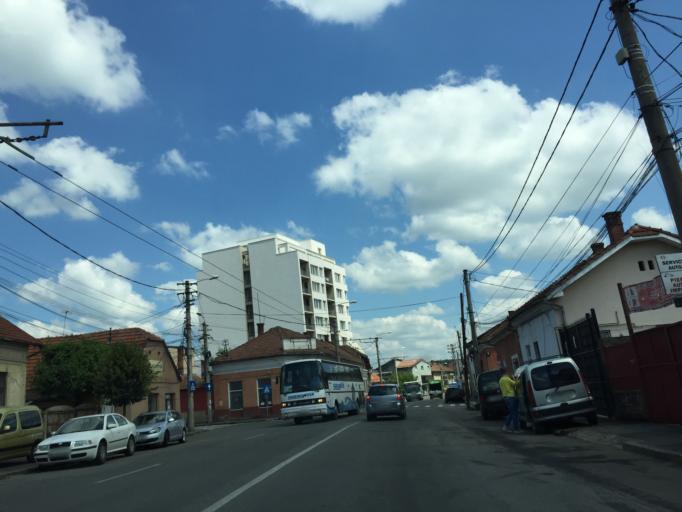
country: RO
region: Cluj
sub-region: Municipiul Cluj-Napoca
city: Cluj-Napoca
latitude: 46.7808
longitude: 23.5918
